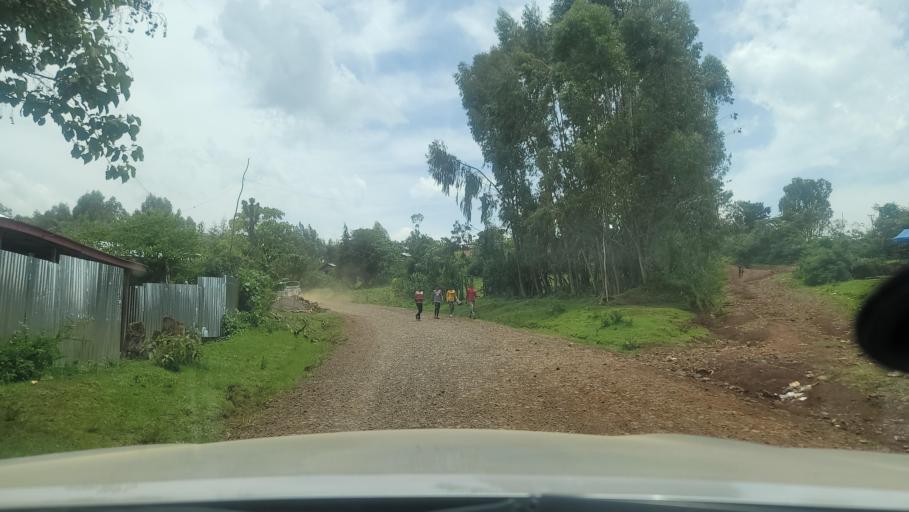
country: ET
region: Oromiya
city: Agaro
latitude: 7.7367
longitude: 36.2586
